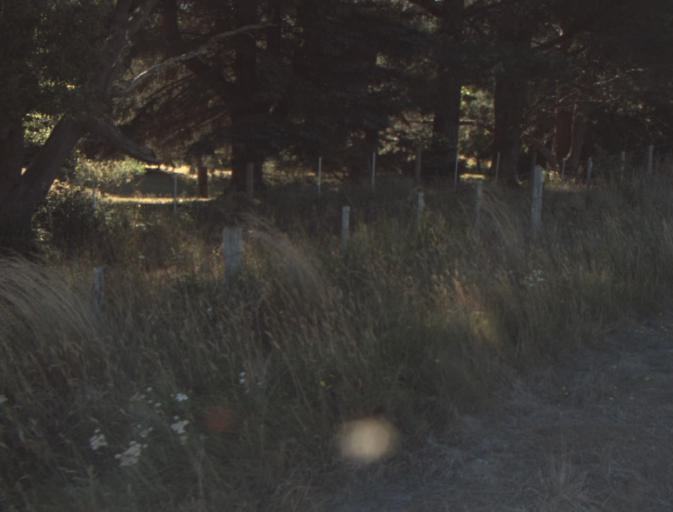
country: AU
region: Tasmania
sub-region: Launceston
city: Newstead
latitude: -41.3318
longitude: 147.3455
